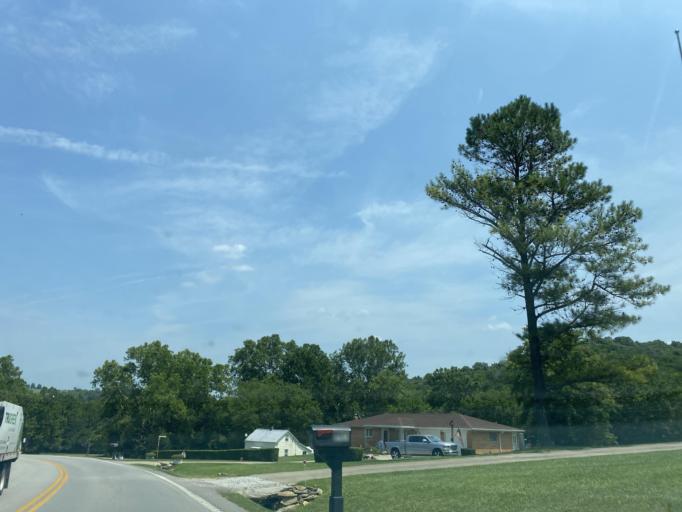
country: US
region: Kentucky
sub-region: Kenton County
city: Ryland Heights
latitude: 38.9223
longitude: -84.4410
